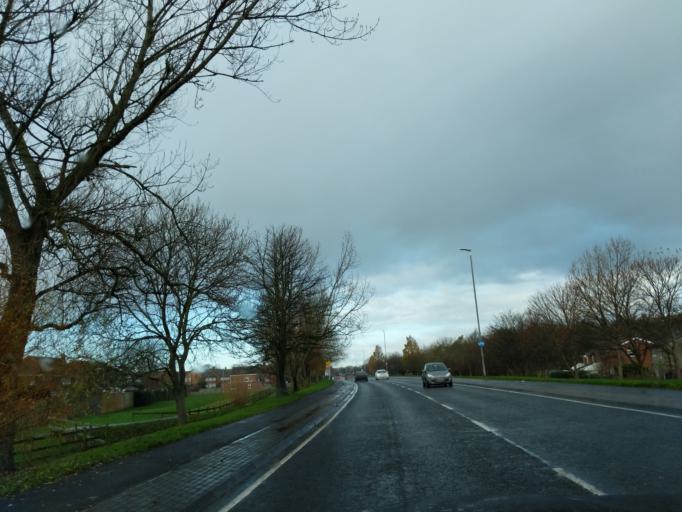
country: GB
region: England
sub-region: Northumberland
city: Blyth
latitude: 55.1165
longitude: -1.5082
